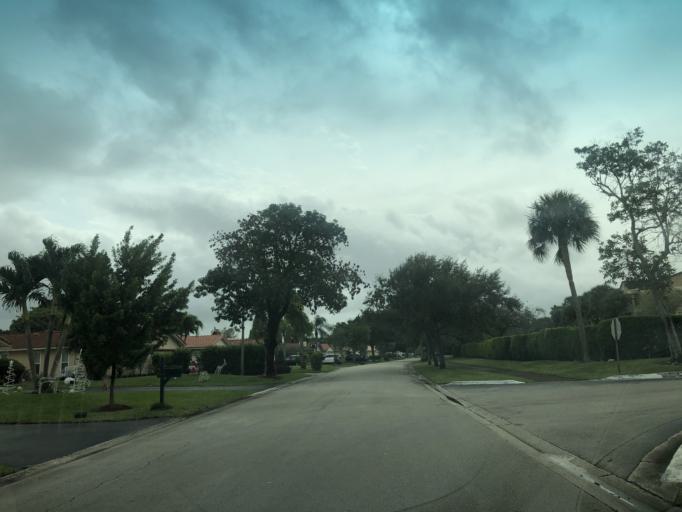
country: US
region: Florida
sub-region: Broward County
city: North Lauderdale
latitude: 26.2419
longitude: -80.2415
